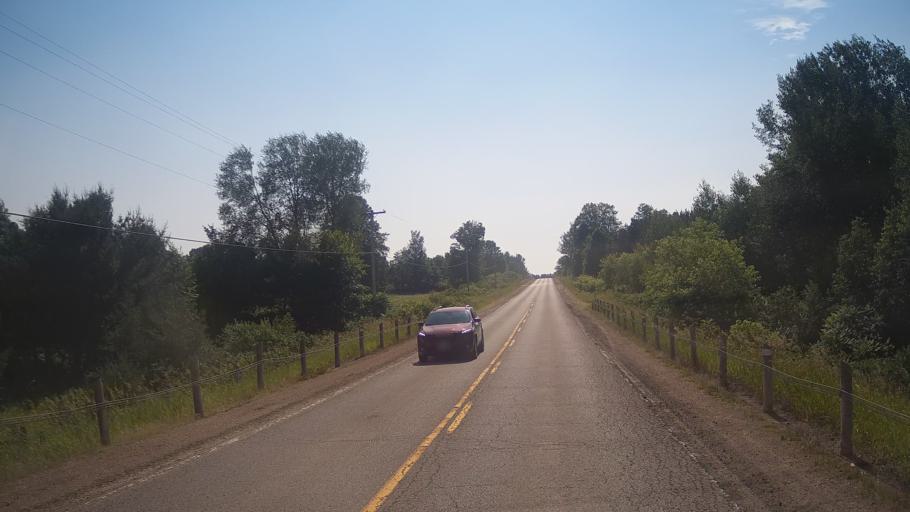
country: CA
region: Ontario
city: Pembroke
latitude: 45.6053
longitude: -77.2223
